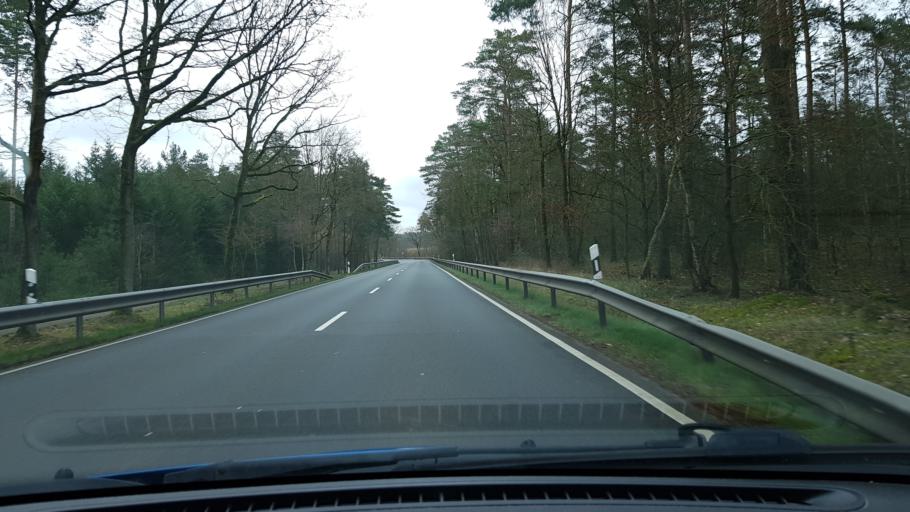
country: DE
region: Lower Saxony
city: Stoetze
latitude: 53.0351
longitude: 10.7840
